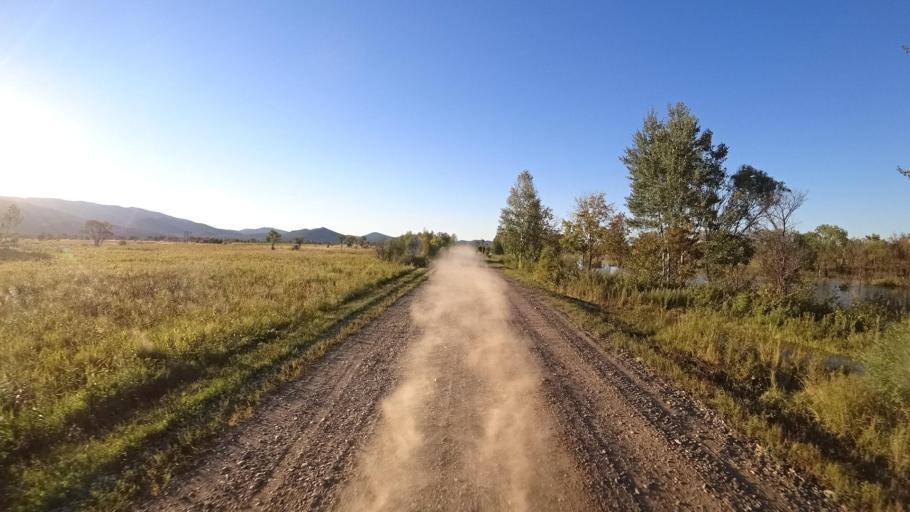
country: RU
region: Primorskiy
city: Kirovskiy
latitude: 44.8066
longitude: 133.6180
